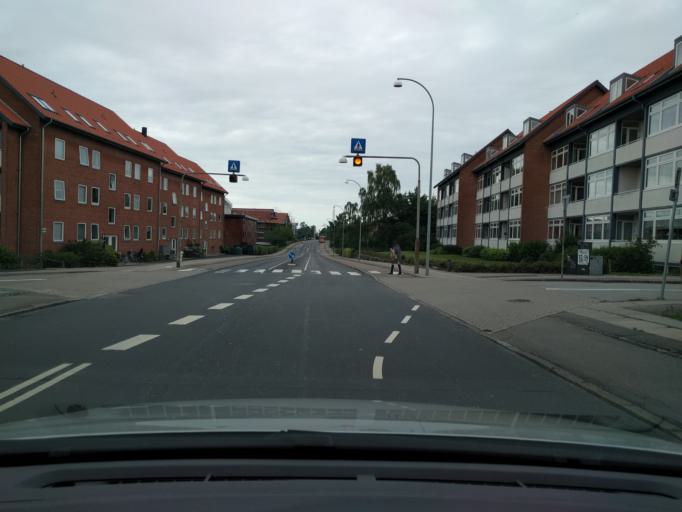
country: DK
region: Zealand
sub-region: Roskilde Kommune
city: Roskilde
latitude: 55.6449
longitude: 12.0670
